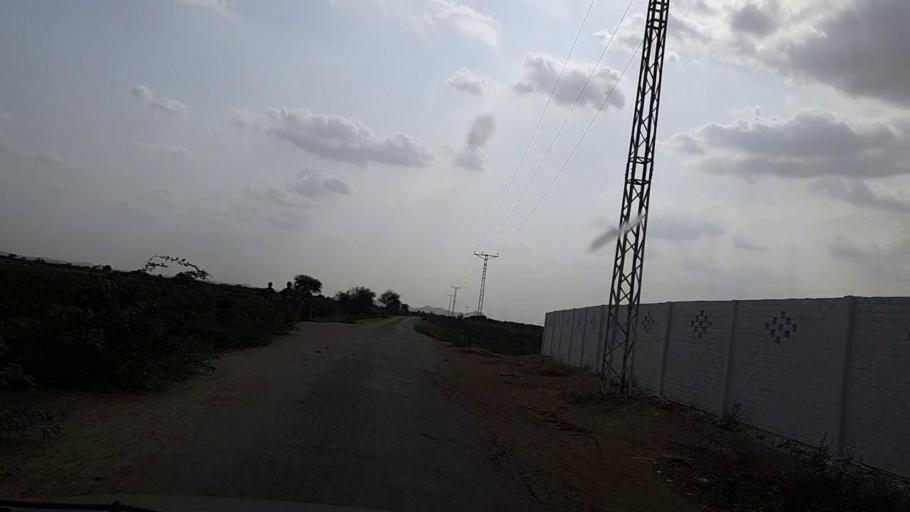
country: PK
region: Sindh
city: Kotri
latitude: 25.2576
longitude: 68.2498
